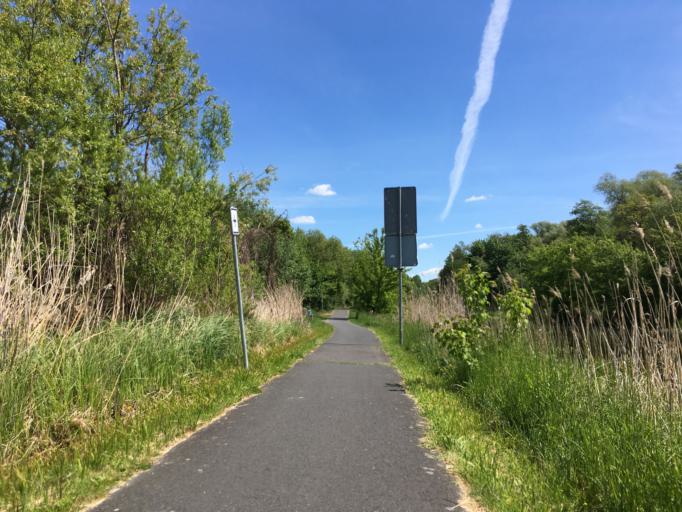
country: DE
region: Brandenburg
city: Eberswalde
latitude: 52.8442
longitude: 13.8369
